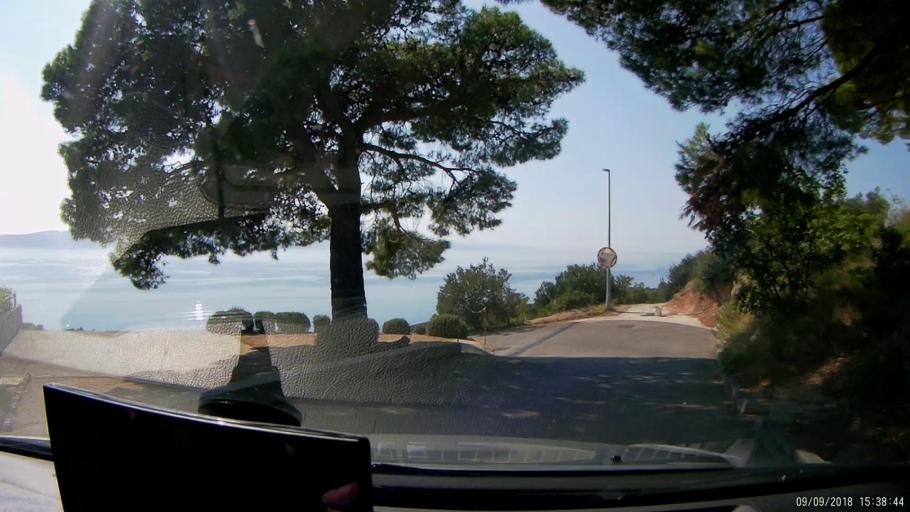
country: HR
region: Splitsko-Dalmatinska
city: Donja Brela
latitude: 43.3699
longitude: 16.9312
